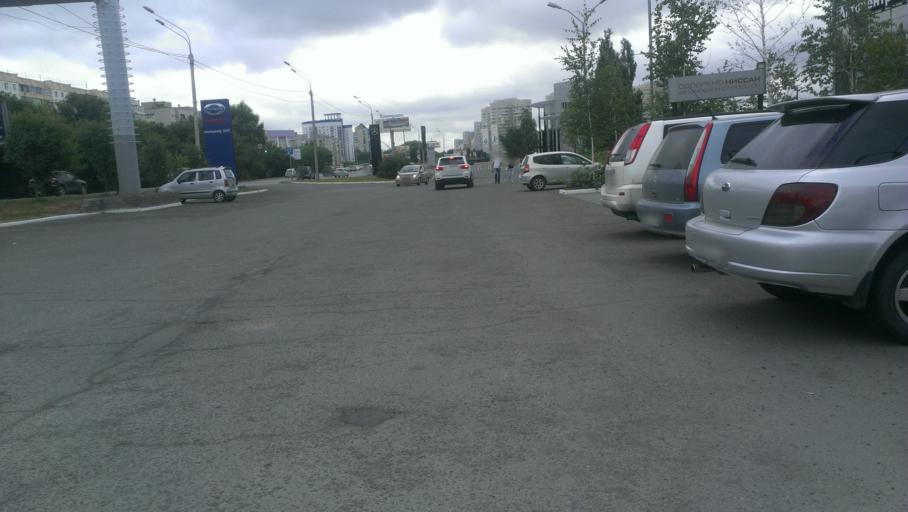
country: RU
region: Altai Krai
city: Novosilikatnyy
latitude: 53.3426
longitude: 83.6884
